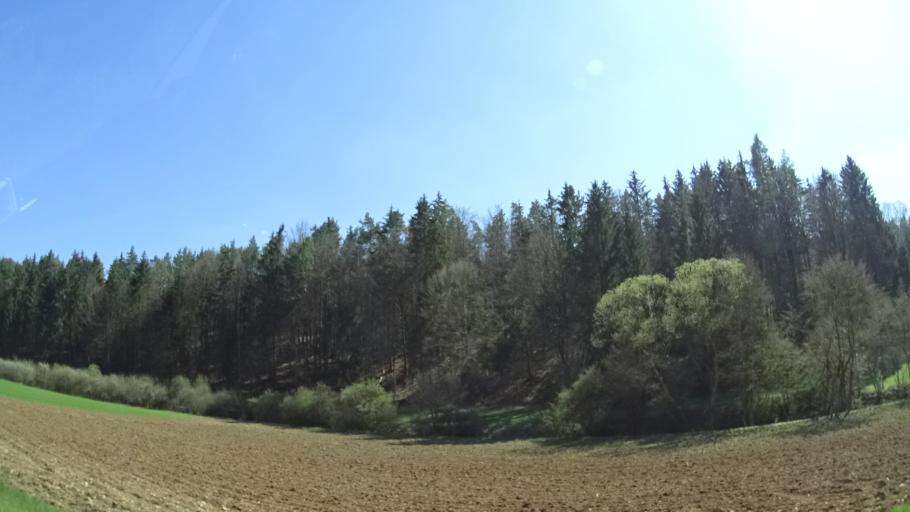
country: DE
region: Bavaria
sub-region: Upper Palatinate
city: Weigendorf
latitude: 49.4855
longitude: 11.6220
